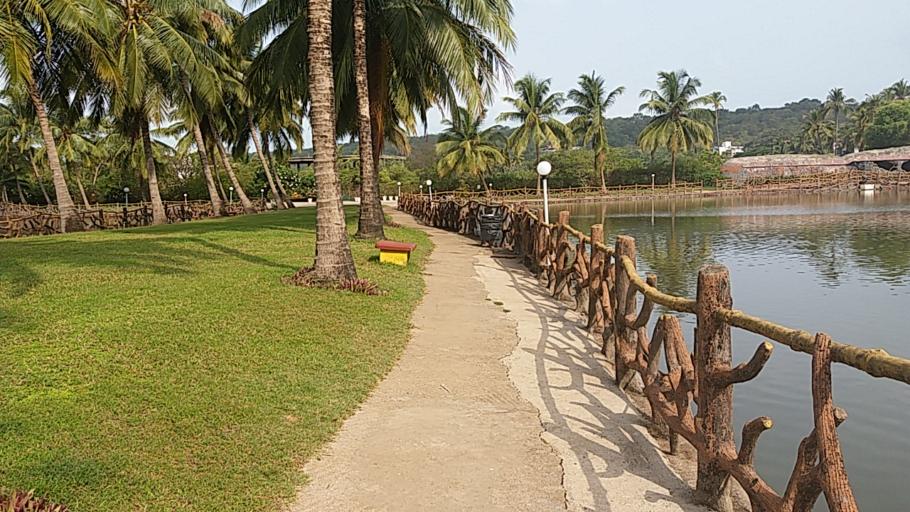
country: IN
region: Goa
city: Calangute
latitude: 15.5673
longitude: 73.7599
